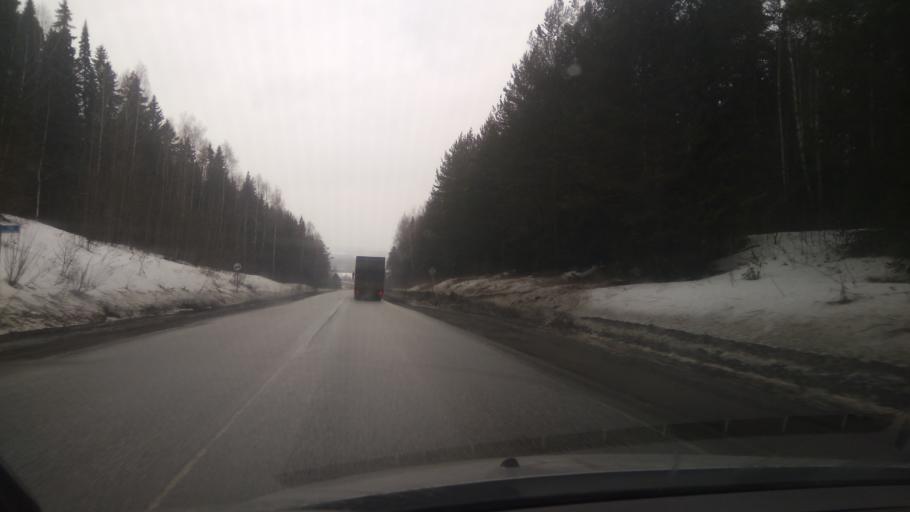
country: RU
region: Perm
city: Kungur
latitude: 57.4443
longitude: 56.8144
